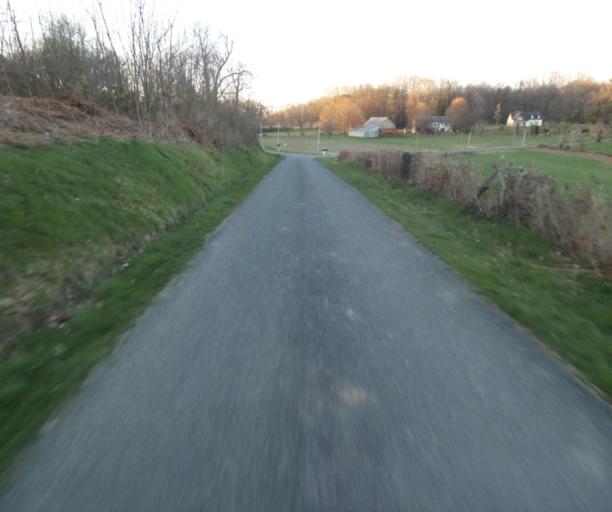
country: FR
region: Limousin
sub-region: Departement de la Correze
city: Uzerche
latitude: 45.3815
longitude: 1.6028
